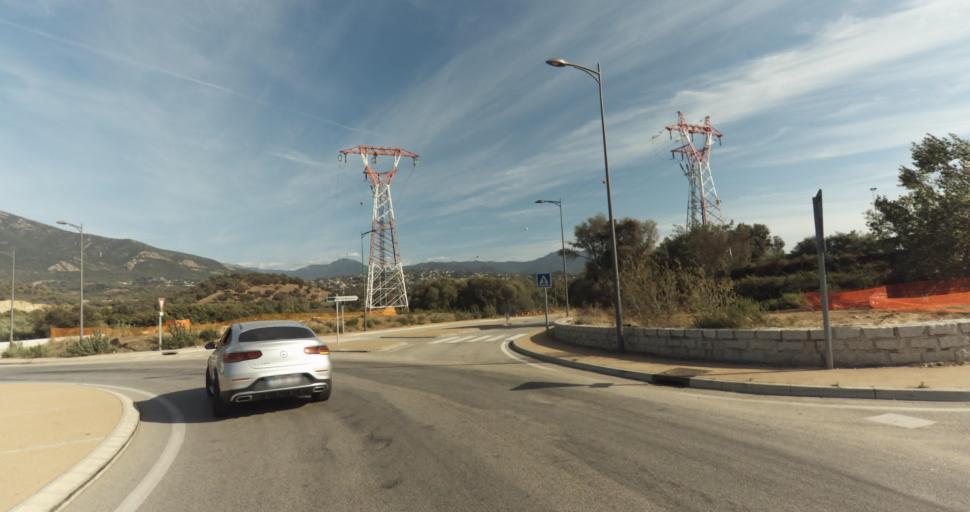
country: FR
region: Corsica
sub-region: Departement de la Corse-du-Sud
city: Afa
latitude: 41.9567
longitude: 8.8129
